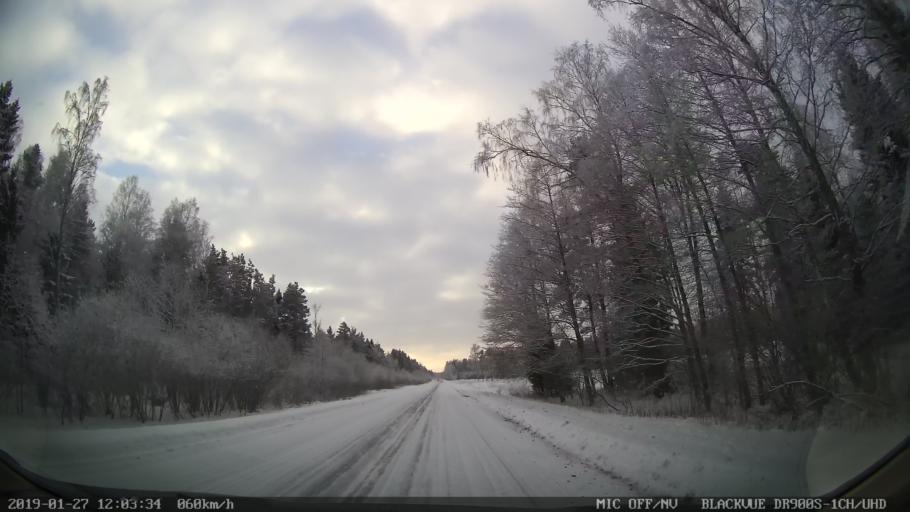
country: EE
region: Harju
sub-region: Raasiku vald
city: Raasiku
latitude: 59.4902
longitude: 25.2617
